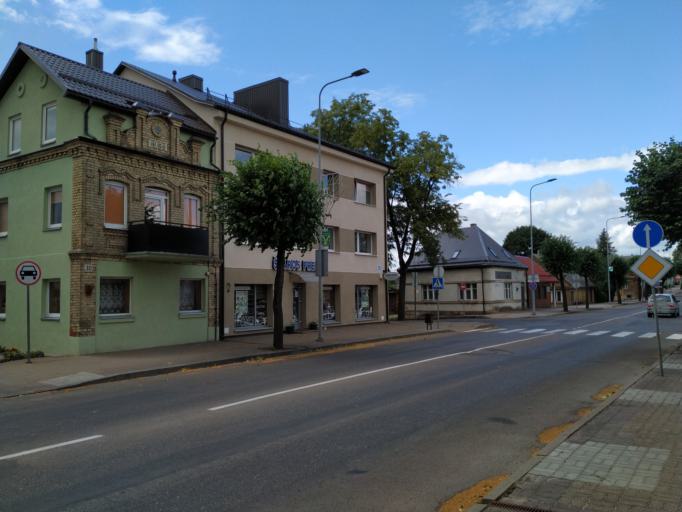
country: LT
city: Kupiskis
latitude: 55.8396
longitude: 24.9764
